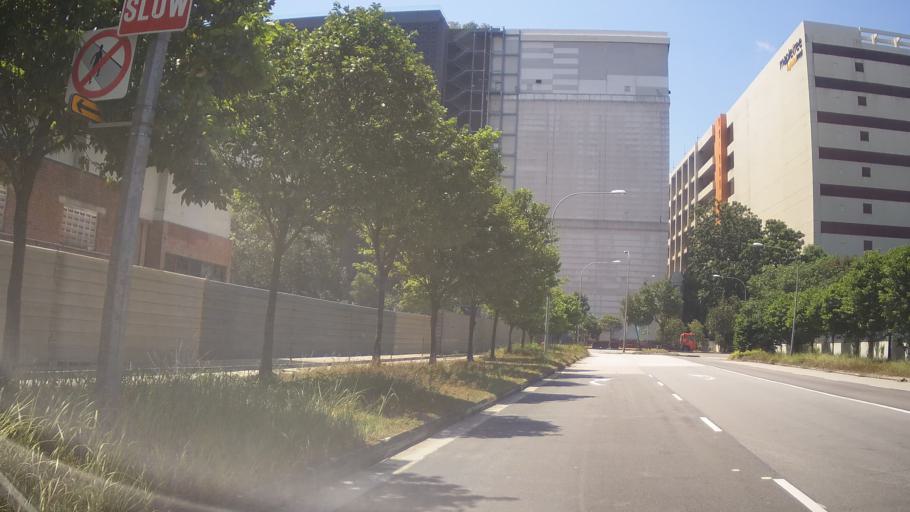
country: SG
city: Singapore
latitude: 1.3148
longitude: 103.7218
